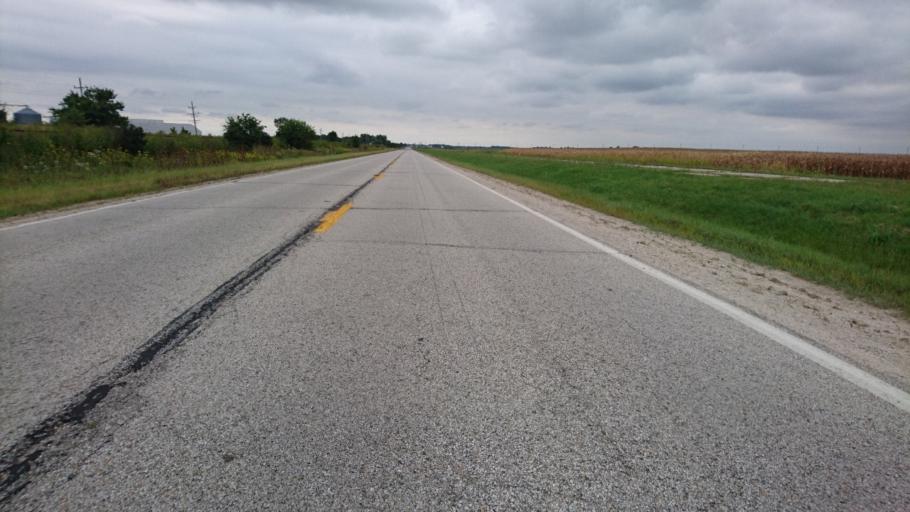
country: US
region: Illinois
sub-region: Livingston County
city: Pontiac
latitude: 40.9285
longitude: -88.5951
